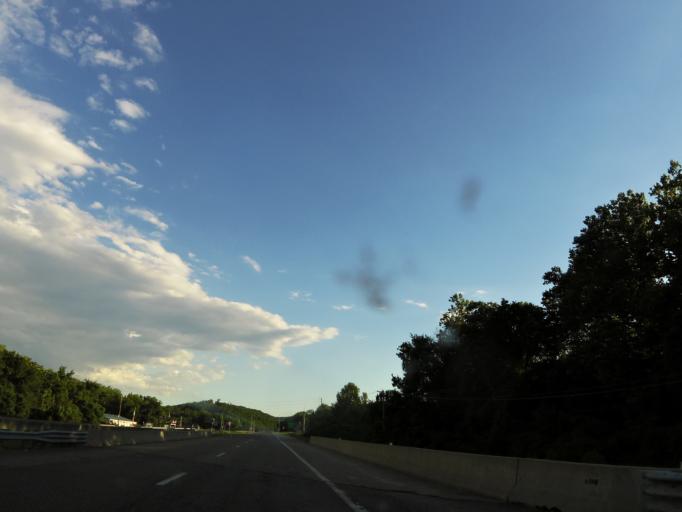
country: US
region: Missouri
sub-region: Jefferson County
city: Byrnes Mill
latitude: 38.4088
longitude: -90.5853
